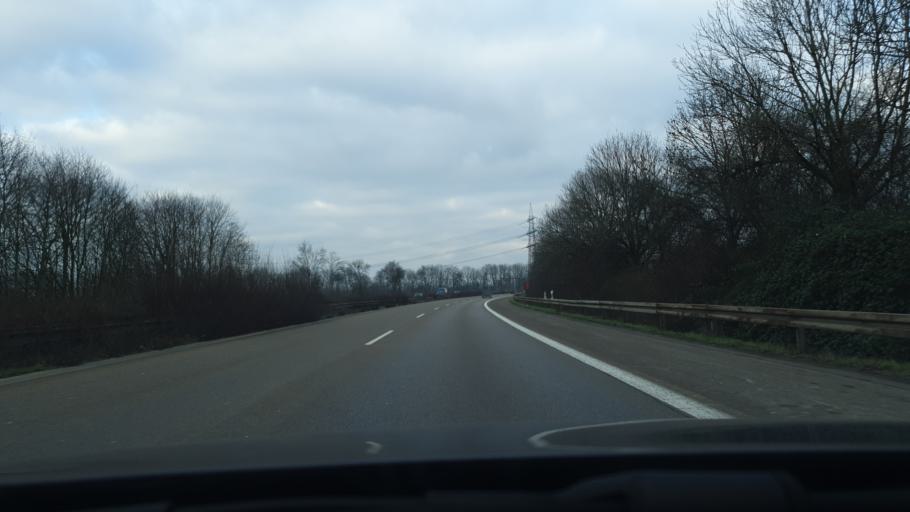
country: DE
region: North Rhine-Westphalia
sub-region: Regierungsbezirk Dusseldorf
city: Krefeld
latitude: 51.3792
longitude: 6.6440
